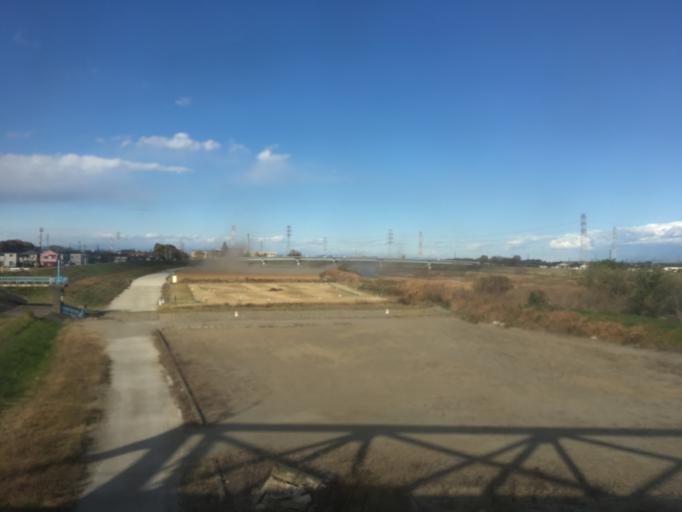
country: JP
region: Saitama
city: Kawagoe
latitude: 35.9237
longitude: 139.4520
